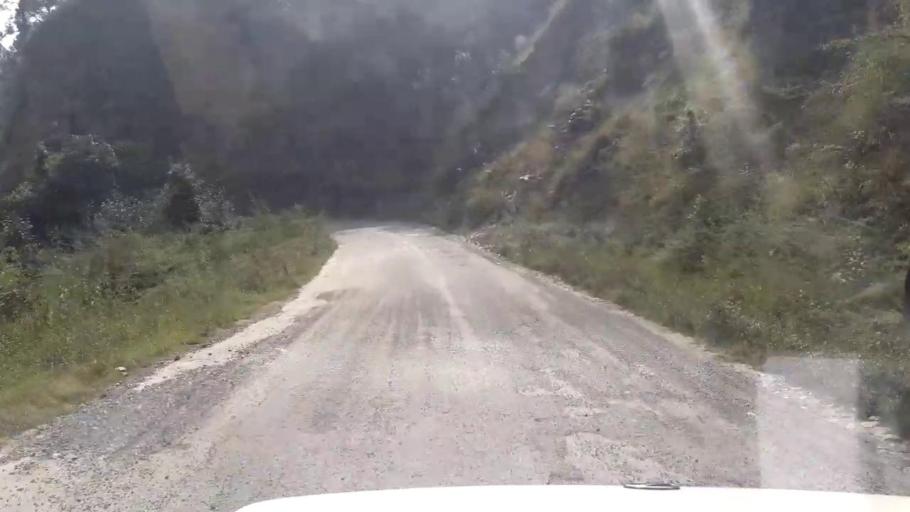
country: IN
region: Himachal Pradesh
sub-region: Shimla
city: Shimla
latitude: 31.0552
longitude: 77.1552
